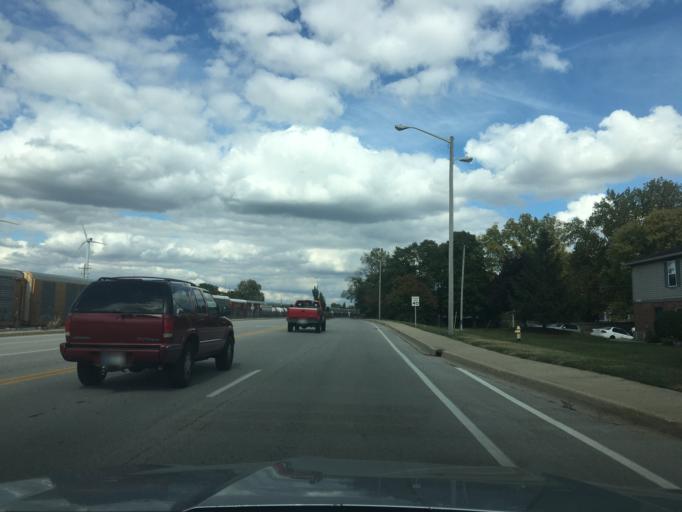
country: US
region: Indiana
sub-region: Tippecanoe County
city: West Lafayette
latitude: 40.4270
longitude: -86.8918
